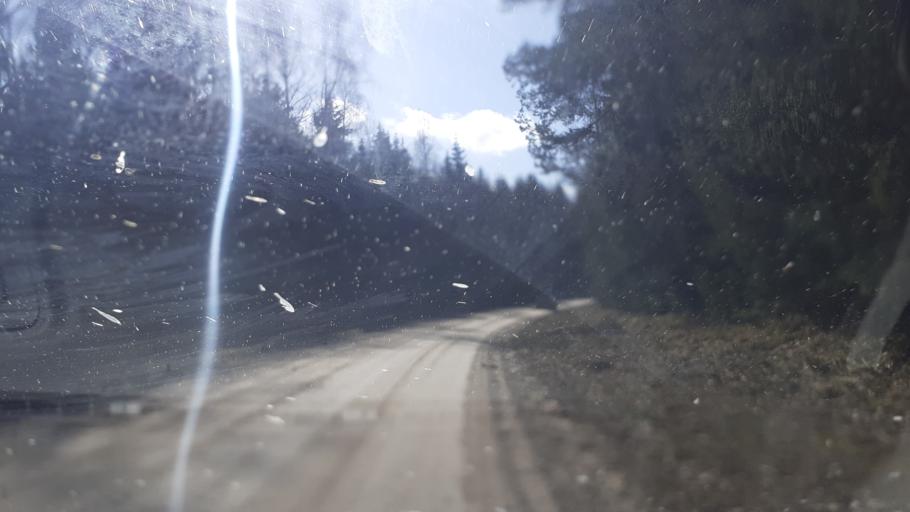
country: LV
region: Kuldigas Rajons
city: Kuldiga
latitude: 56.9118
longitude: 22.0839
